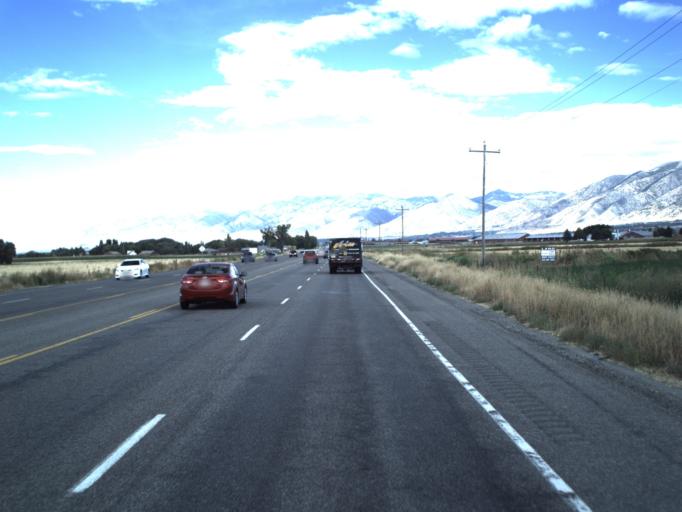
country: US
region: Utah
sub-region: Cache County
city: Wellsville
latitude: 41.6503
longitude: -111.9085
